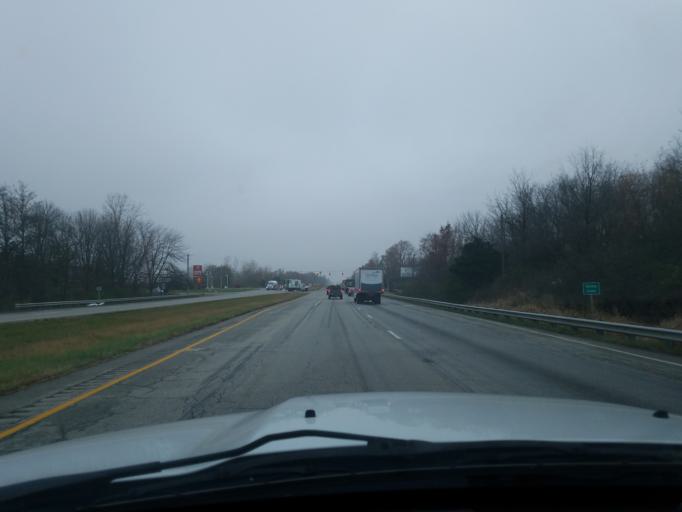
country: US
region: Indiana
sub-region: Hamilton County
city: Westfield
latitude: 40.1298
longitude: -86.1280
